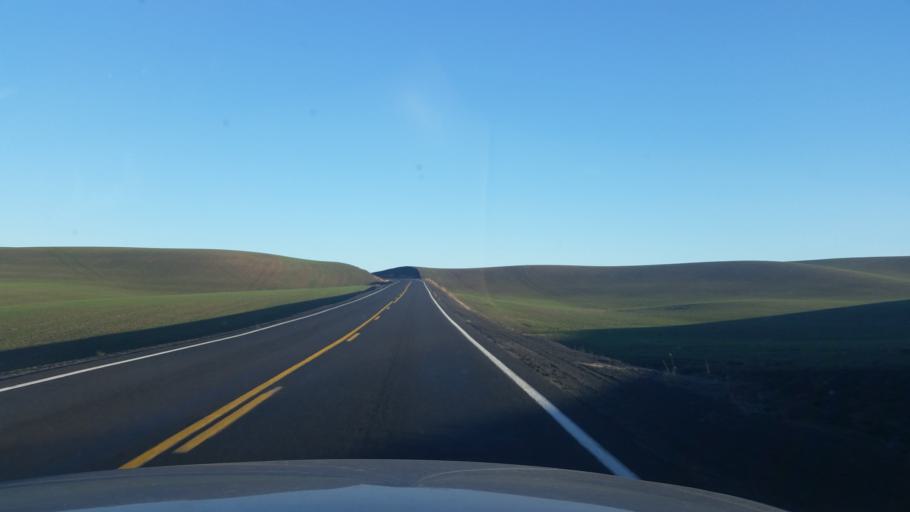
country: US
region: Washington
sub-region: Spokane County
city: Opportunity
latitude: 47.3587
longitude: -117.2754
